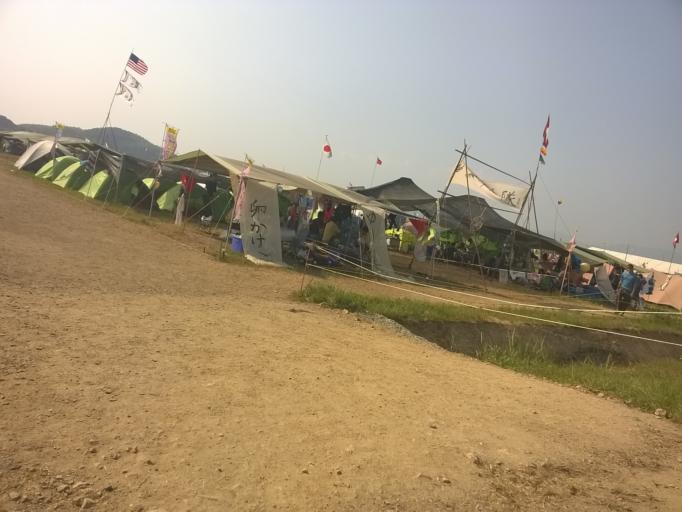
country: JP
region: Yamaguchi
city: Ogori-shimogo
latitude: 34.0170
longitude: 131.3740
